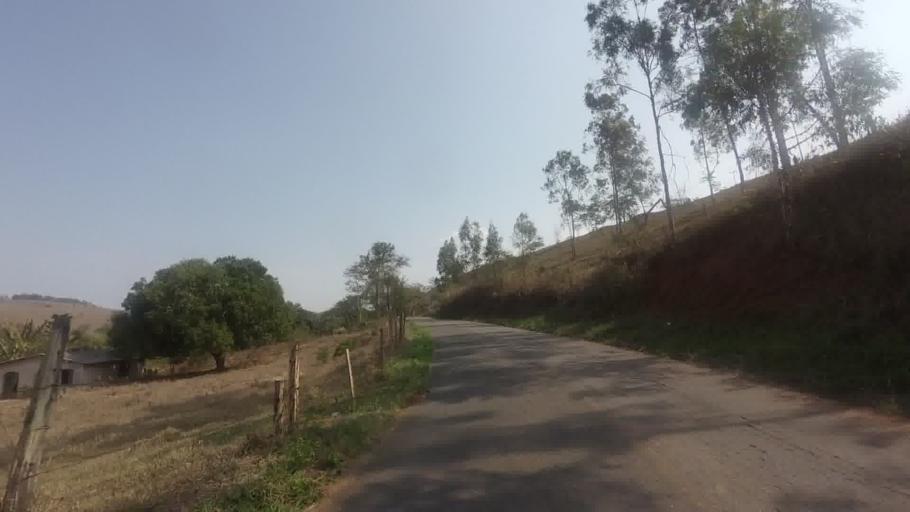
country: BR
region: Rio de Janeiro
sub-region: Bom Jesus Do Itabapoana
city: Bom Jesus do Itabapoana
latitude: -21.1388
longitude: -41.5684
